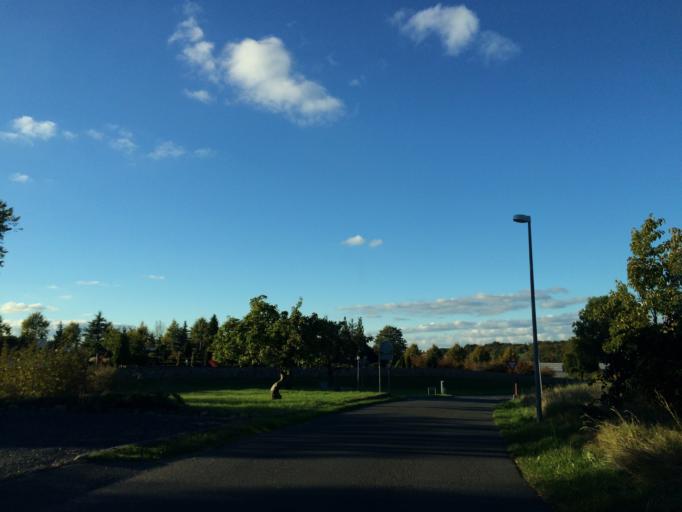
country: DK
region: Central Jutland
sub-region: Silkeborg Kommune
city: Svejbaek
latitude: 56.1552
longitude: 9.6920
